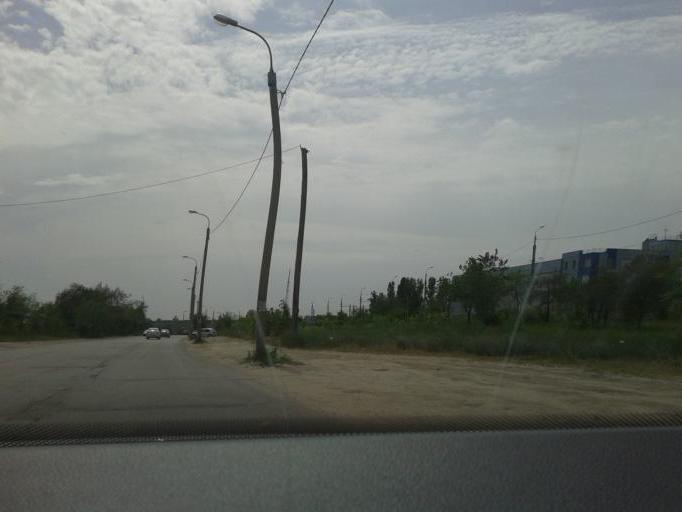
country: RU
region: Volgograd
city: Volgograd
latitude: 48.7606
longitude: 44.5212
